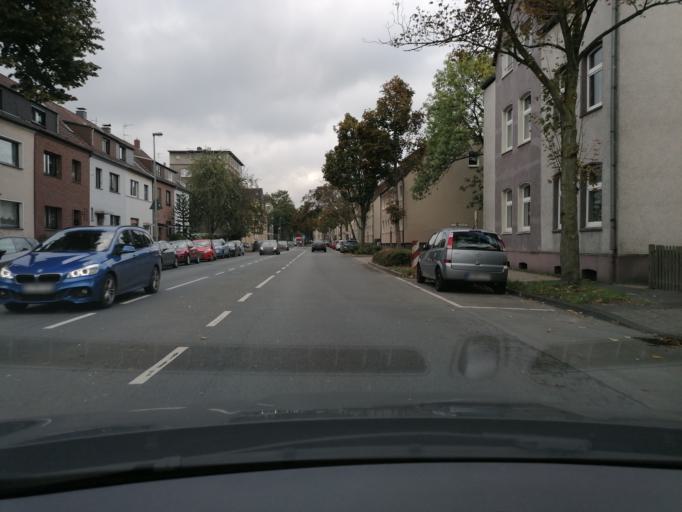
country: DE
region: North Rhine-Westphalia
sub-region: Regierungsbezirk Munster
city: Gelsenkirchen
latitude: 51.5362
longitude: 7.1495
